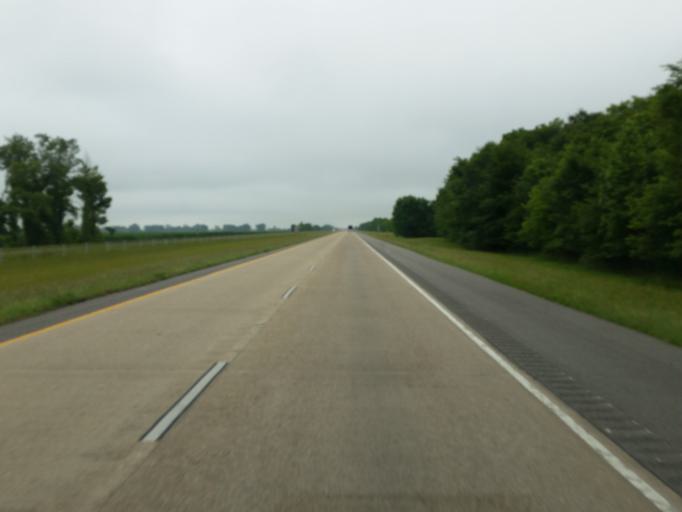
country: US
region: Louisiana
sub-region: Madison Parish
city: Tallulah
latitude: 32.3340
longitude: -91.0503
